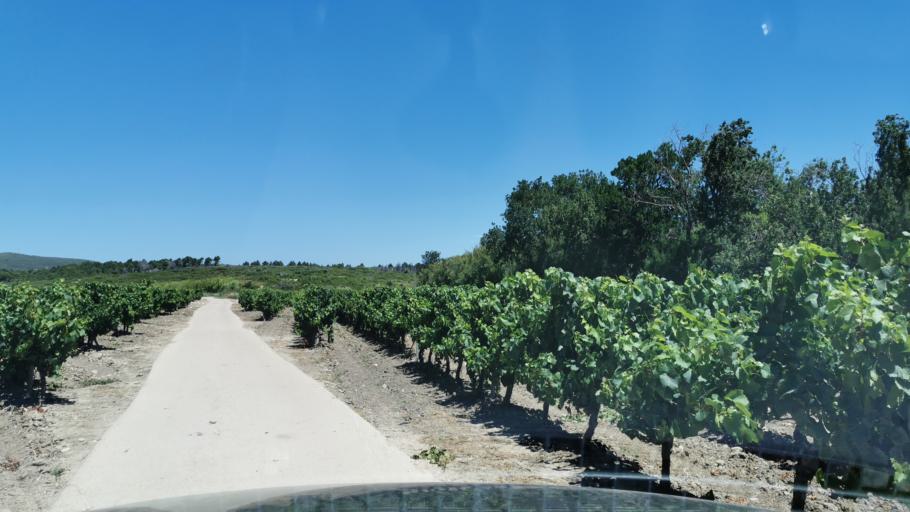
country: FR
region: Languedoc-Roussillon
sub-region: Departement de l'Aude
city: Peyriac-de-Mer
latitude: 43.1035
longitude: 2.9592
